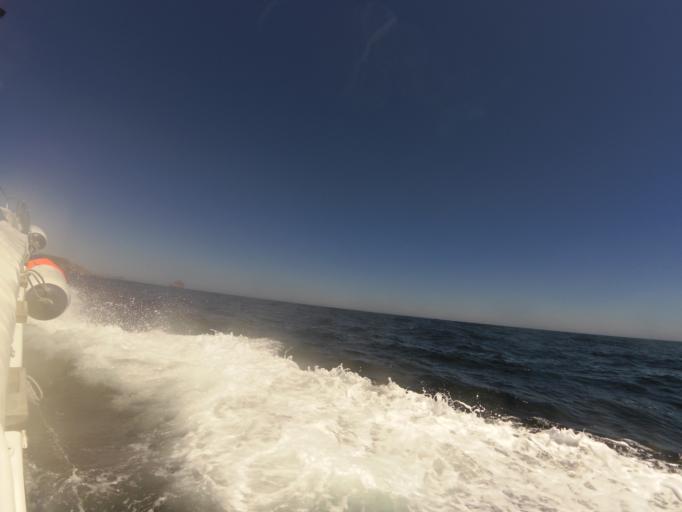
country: PT
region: Leiria
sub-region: Peniche
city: Peniche
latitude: 39.4009
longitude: -9.4882
